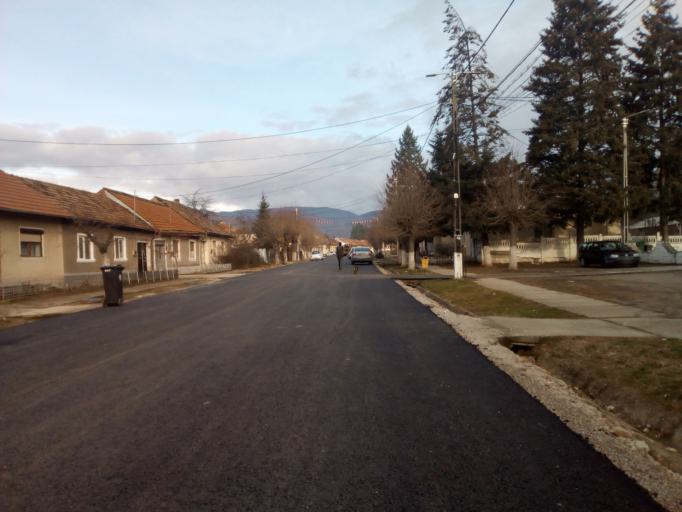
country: RO
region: Mehedinti
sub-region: Comuna Eselnita
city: Eselnita
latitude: 44.6983
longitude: 22.3647
